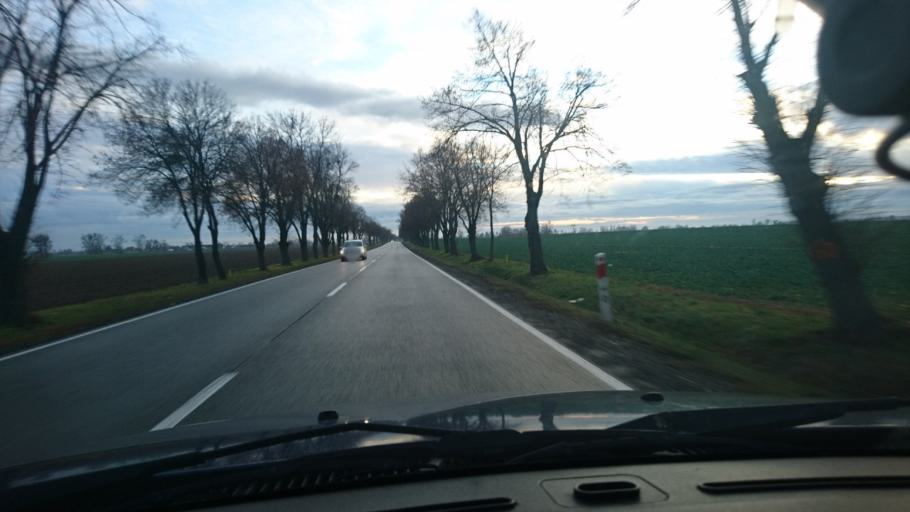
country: PL
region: Opole Voivodeship
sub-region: Powiat kluczborski
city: Kluczbork
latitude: 51.0413
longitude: 18.1949
